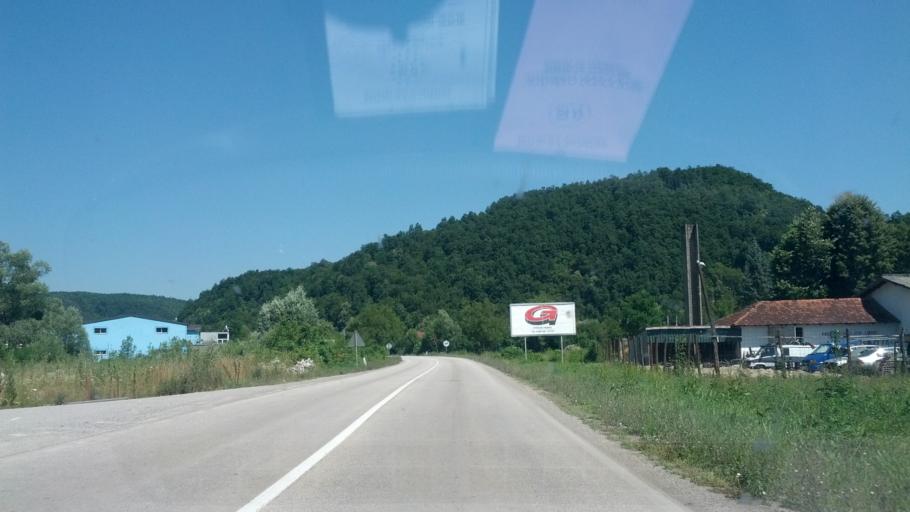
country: BA
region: Federation of Bosnia and Herzegovina
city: Bosanska Krupa
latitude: 44.9102
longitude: 16.1578
